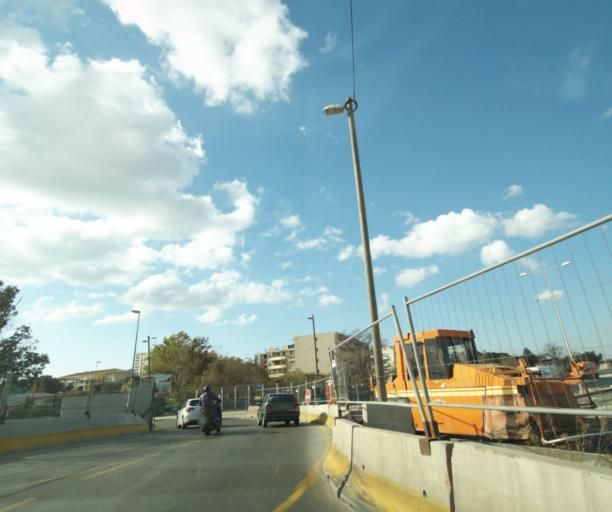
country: FR
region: Provence-Alpes-Cote d'Azur
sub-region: Departement des Bouches-du-Rhone
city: Marseille 14
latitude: 43.3306
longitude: 5.3883
